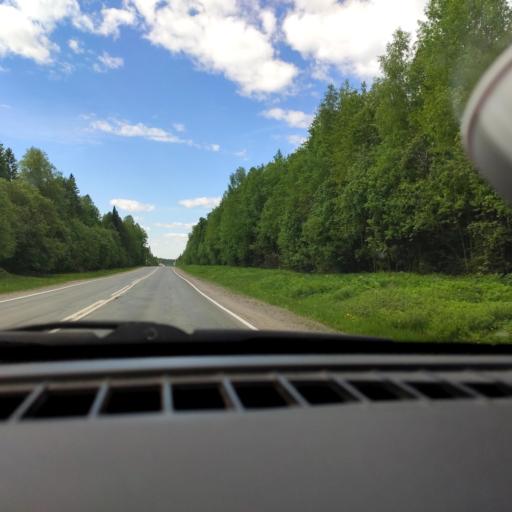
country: RU
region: Perm
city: Perm
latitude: 58.1850
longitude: 56.2207
